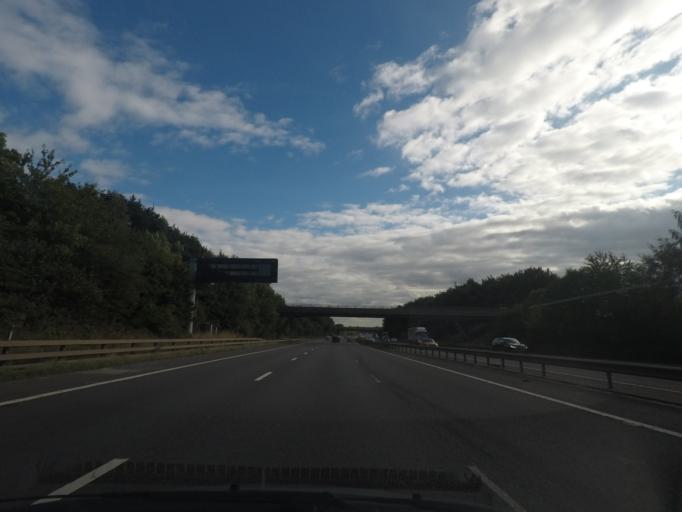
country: GB
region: England
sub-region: Leicestershire
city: Markfield
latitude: 52.6888
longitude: -1.2897
